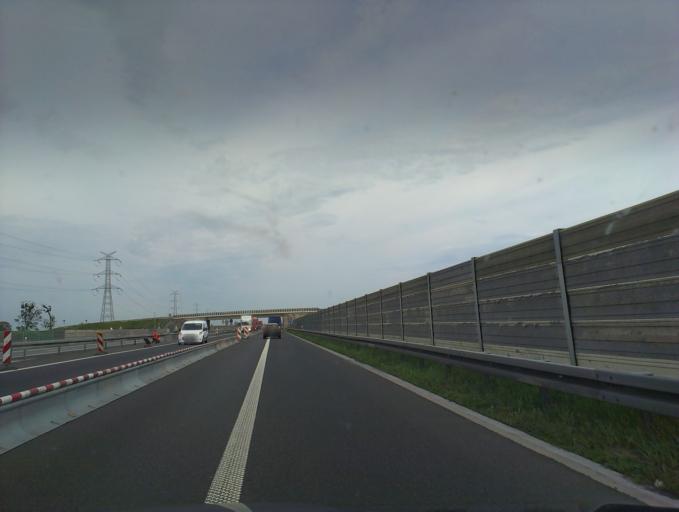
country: PL
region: Opole Voivodeship
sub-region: Powiat brzeski
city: Losiow
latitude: 50.7202
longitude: 17.5401
